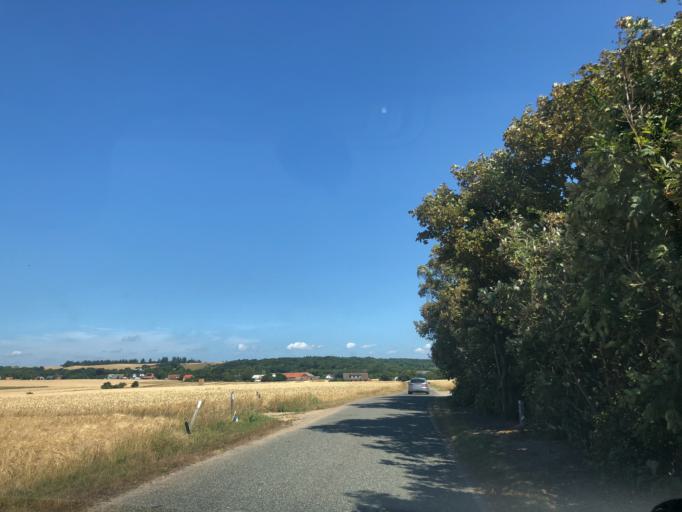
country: DK
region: North Denmark
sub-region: Morso Kommune
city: Nykobing Mors
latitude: 56.8155
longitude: 8.9967
